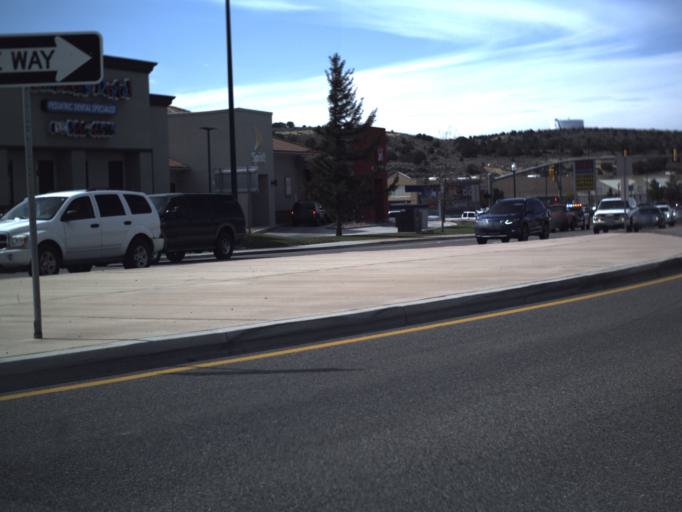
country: US
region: Utah
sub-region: Iron County
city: Cedar City
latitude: 37.6549
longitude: -113.0836
